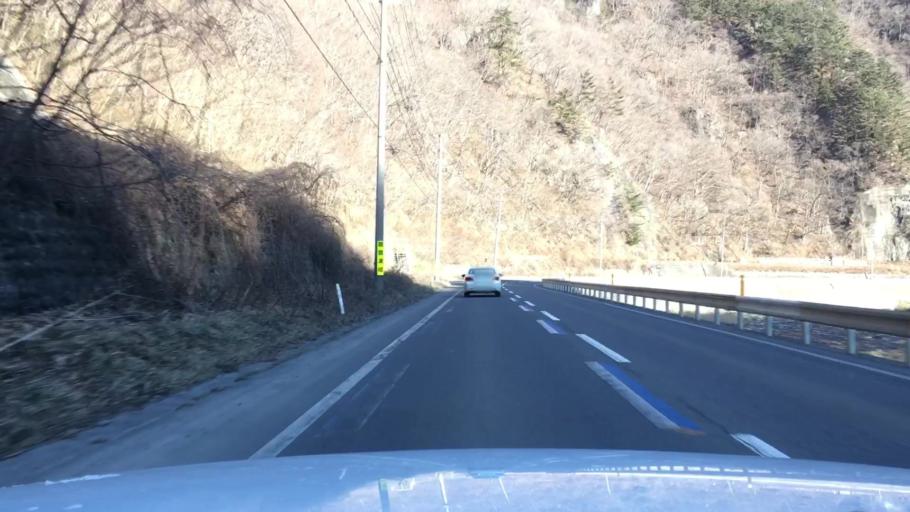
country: JP
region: Iwate
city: Miyako
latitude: 39.6091
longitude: 141.7731
